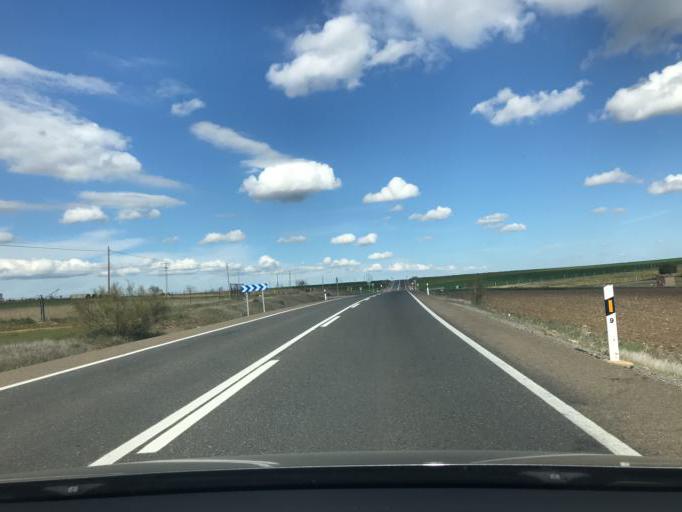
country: ES
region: Extremadura
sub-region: Provincia de Badajoz
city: Azuaga
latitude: 38.2850
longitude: -5.6596
